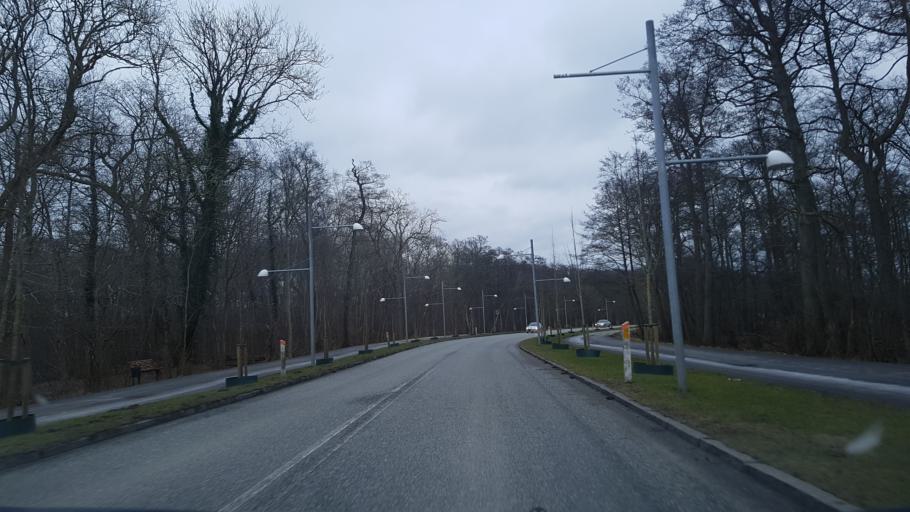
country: DK
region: Zealand
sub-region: Soro Kommune
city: Soro
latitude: 55.4285
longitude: 11.5633
